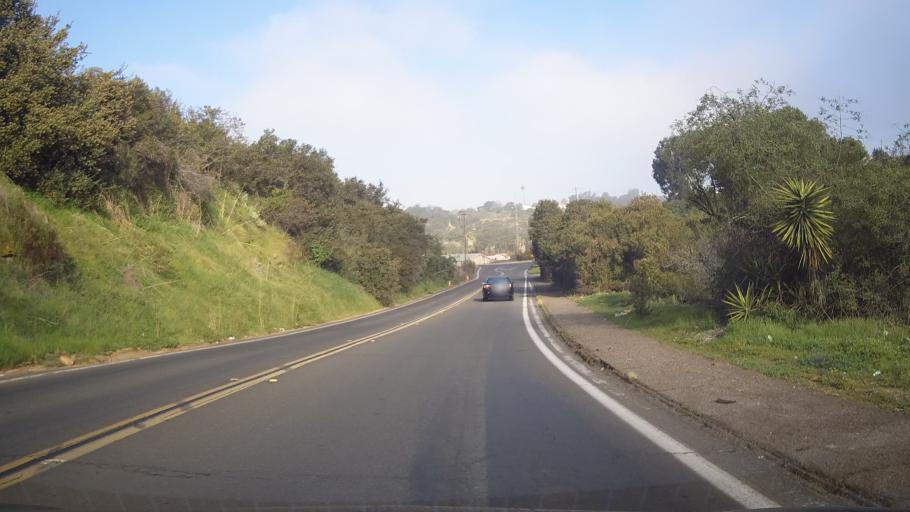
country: US
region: California
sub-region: San Diego County
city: National City
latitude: 32.7278
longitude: -117.0875
